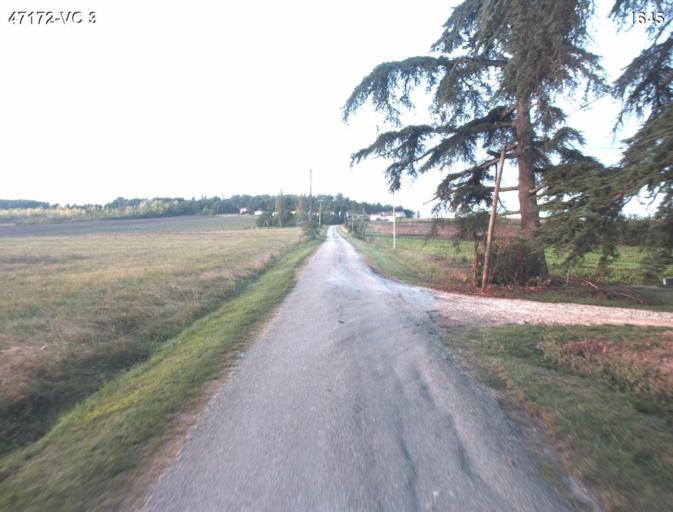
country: FR
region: Aquitaine
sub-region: Departement du Lot-et-Garonne
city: Sainte-Colombe-en-Bruilhois
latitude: 44.1560
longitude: 0.4939
